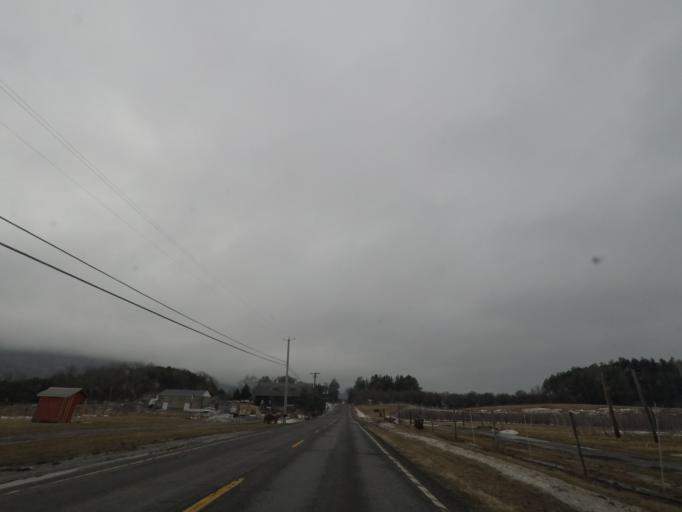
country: US
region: New York
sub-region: Albany County
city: Voorheesville
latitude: 42.6552
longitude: -73.9708
